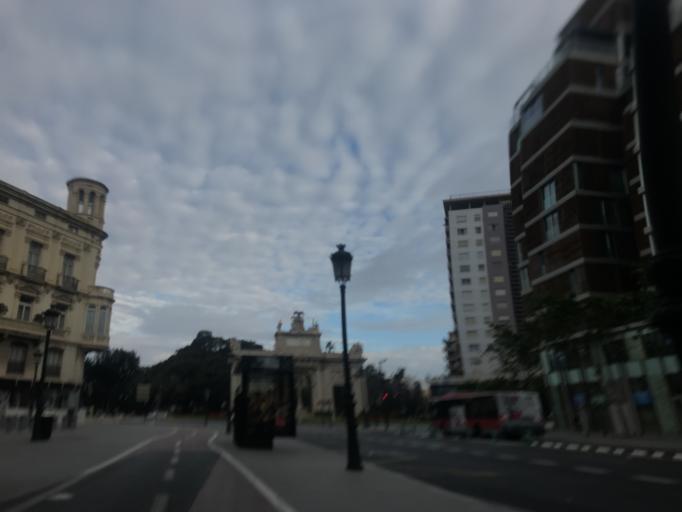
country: ES
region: Valencia
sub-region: Provincia de Valencia
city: Valencia
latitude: 39.4715
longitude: -0.3671
